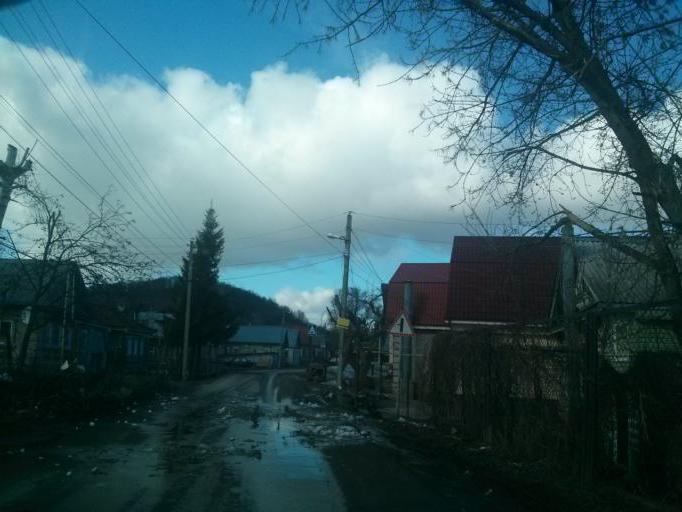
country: RU
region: Nizjnij Novgorod
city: Afonino
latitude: 56.2915
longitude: 44.0999
